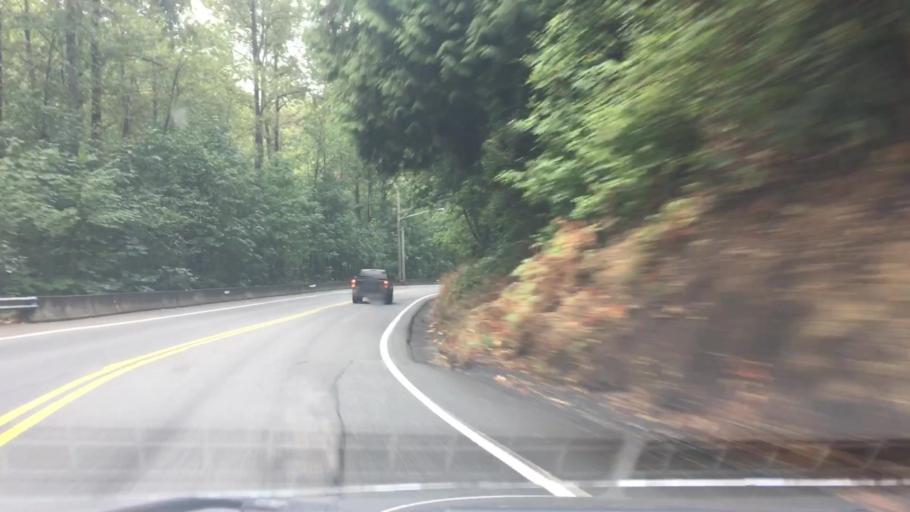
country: CA
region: British Columbia
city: Langley
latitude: 49.1036
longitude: -122.5443
